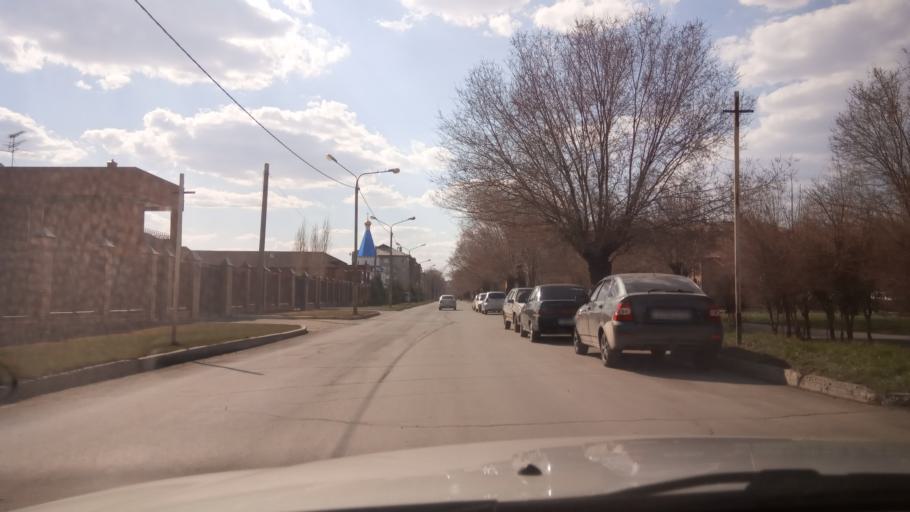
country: RU
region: Orenburg
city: Novotroitsk
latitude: 51.1940
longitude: 58.3108
